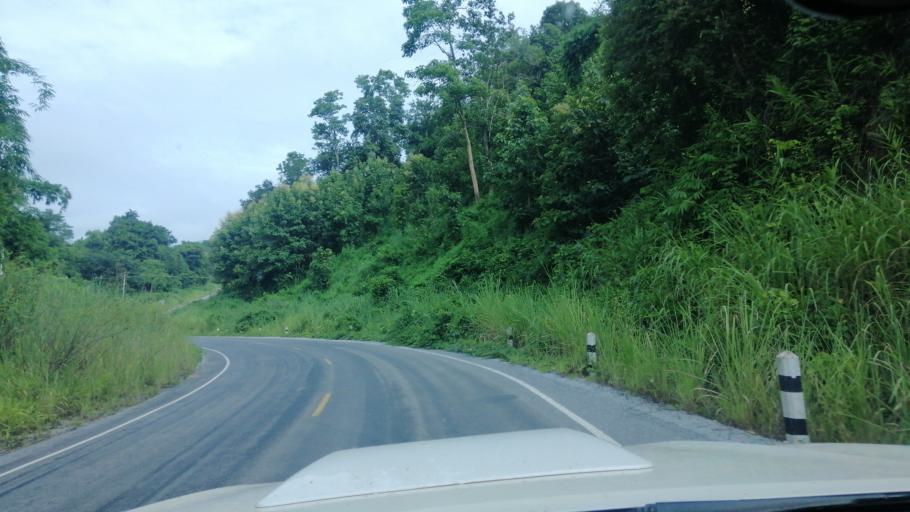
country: TH
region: Phayao
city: Phu Sang
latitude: 19.6777
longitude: 100.4341
